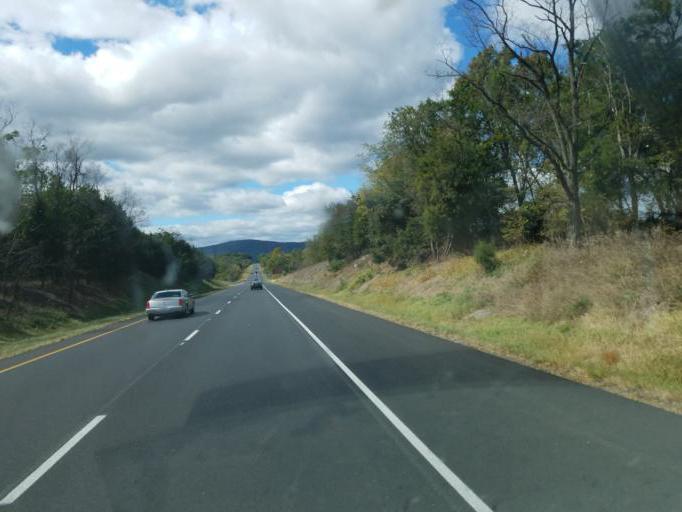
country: US
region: Maryland
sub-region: Washington County
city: Wilson-Conococheague
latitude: 39.6522
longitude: -77.8932
